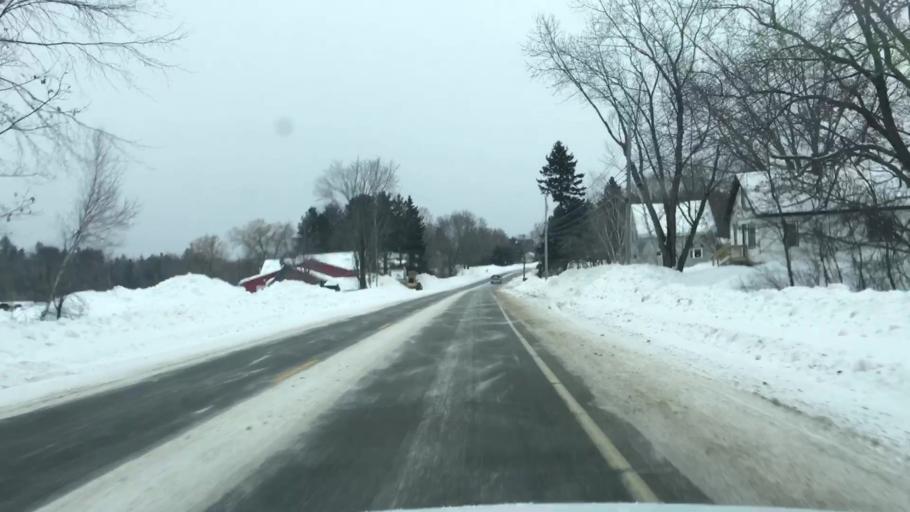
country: US
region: Maine
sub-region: Penobscot County
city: Lincoln
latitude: 45.3998
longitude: -68.4911
